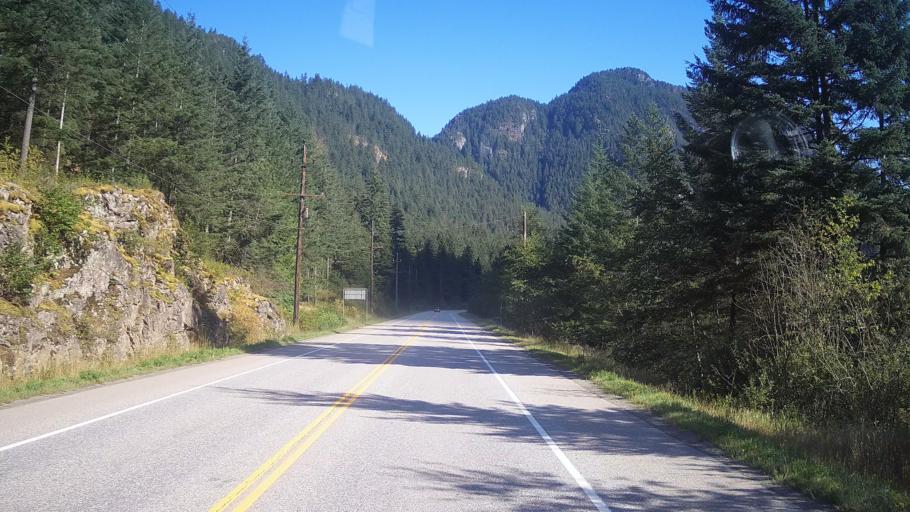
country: CA
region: British Columbia
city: Hope
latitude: 49.5983
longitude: -121.4145
